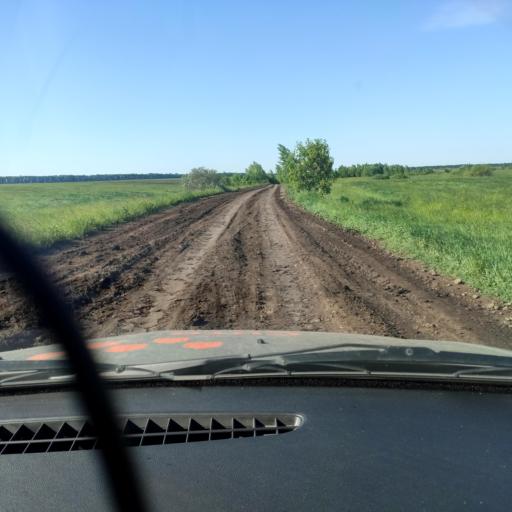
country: RU
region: Bashkortostan
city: Avdon
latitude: 54.5760
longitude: 55.8438
